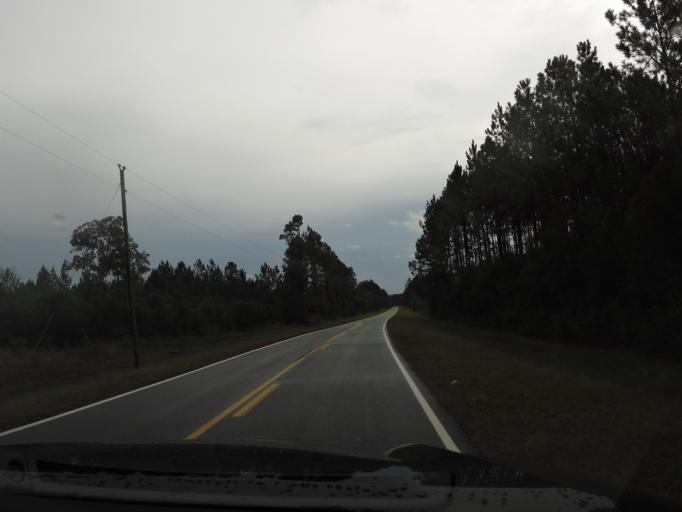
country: US
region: Georgia
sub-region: Wayne County
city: Jesup
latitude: 31.5512
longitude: -81.8762
